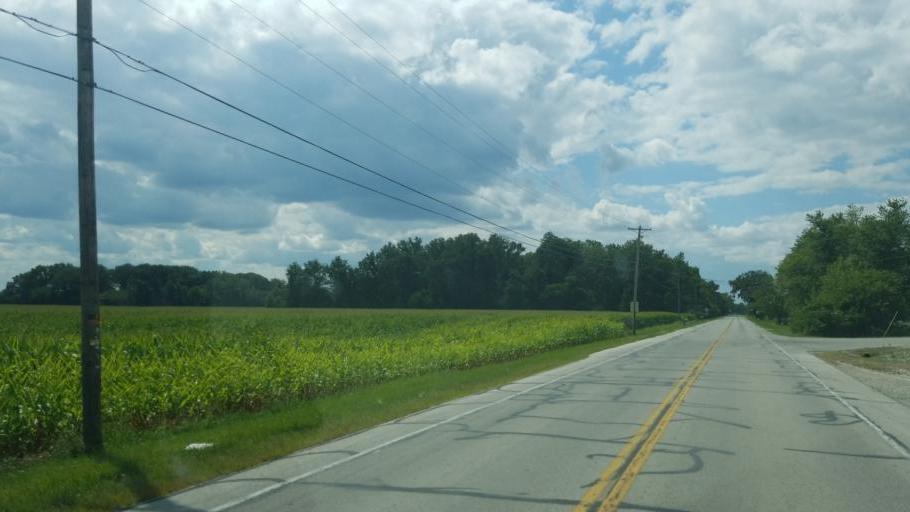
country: US
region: Ohio
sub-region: Lucas County
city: Curtice
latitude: 41.6609
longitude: -83.2855
